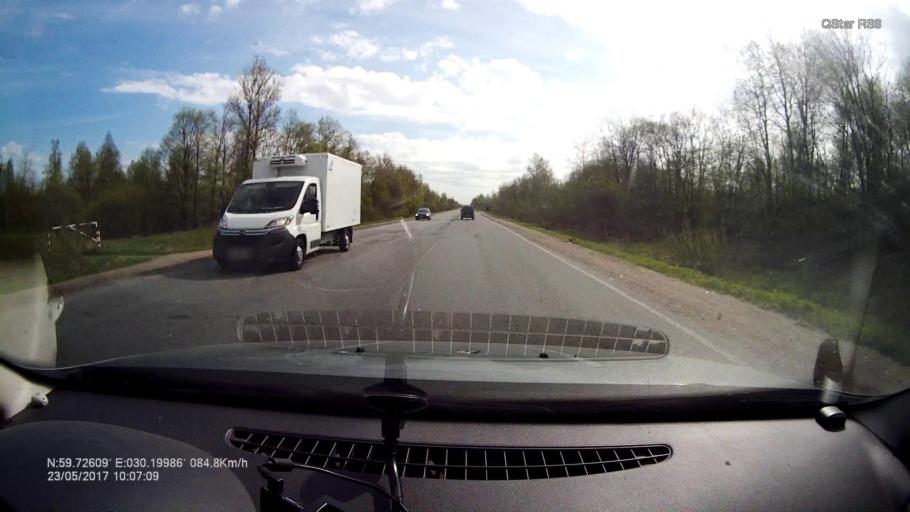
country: RU
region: St.-Petersburg
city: Gorelovo
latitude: 59.7261
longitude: 30.2005
